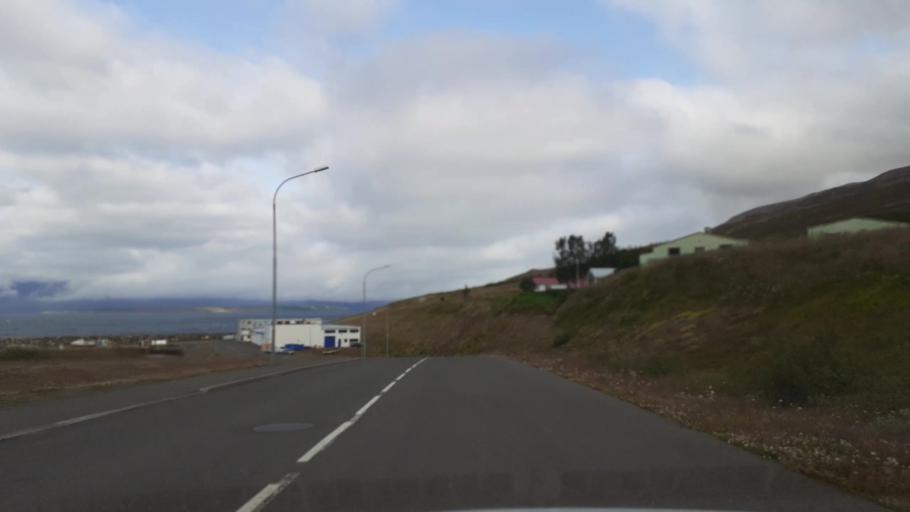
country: IS
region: Northeast
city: Akureyri
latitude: 65.9529
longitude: -18.1798
